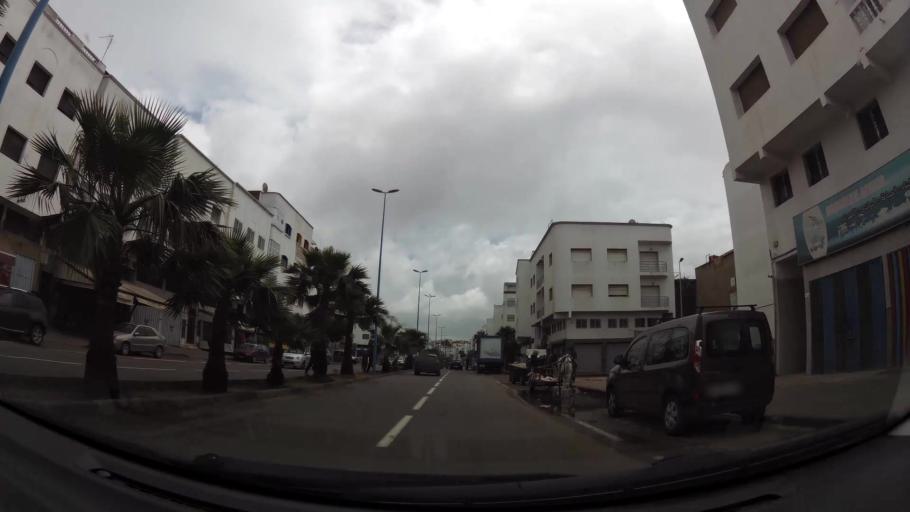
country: MA
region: Grand Casablanca
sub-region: Casablanca
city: Casablanca
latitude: 33.5430
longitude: -7.6848
